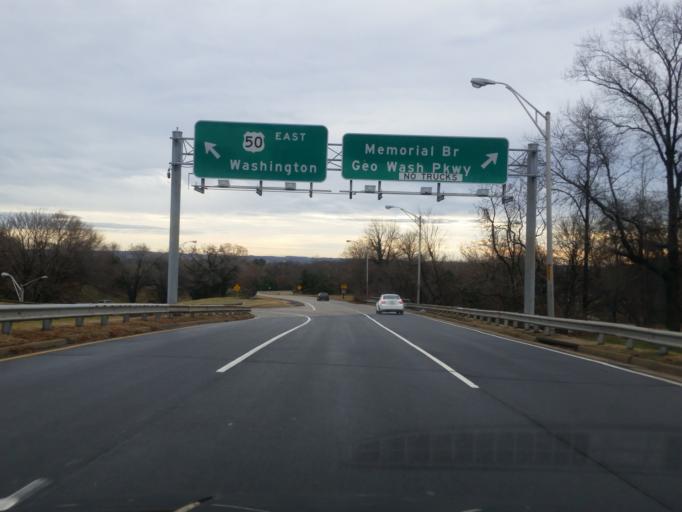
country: US
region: Washington, D.C.
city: Washington, D.C.
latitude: 38.8908
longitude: -77.0686
